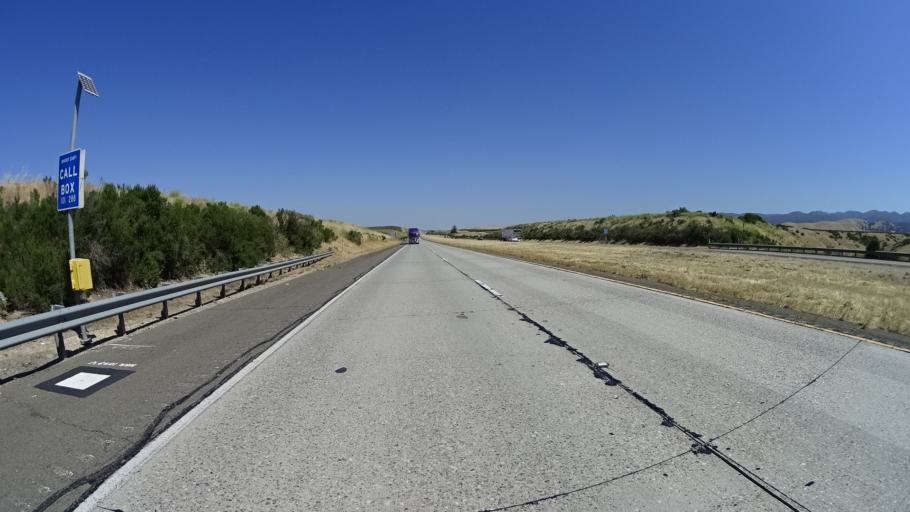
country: US
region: California
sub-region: Monterey County
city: King City
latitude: 36.0847
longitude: -121.0083
